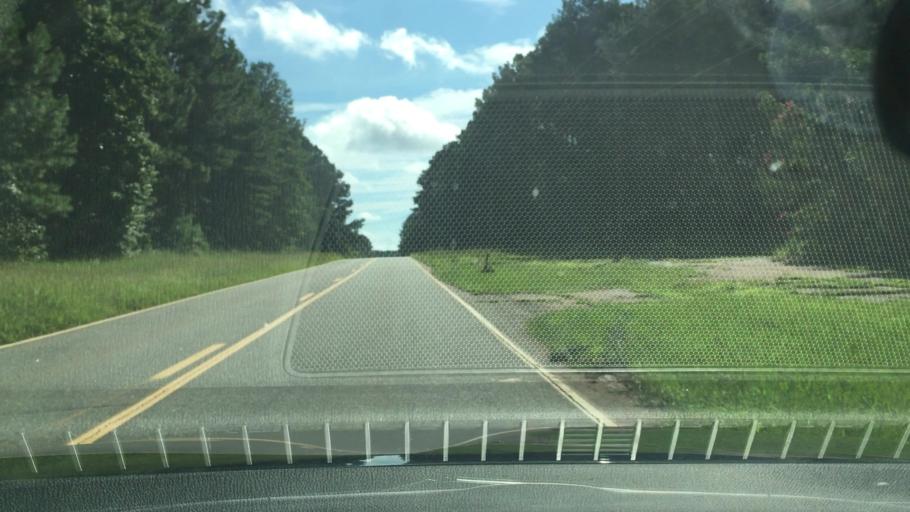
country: US
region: Georgia
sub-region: Putnam County
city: Jefferson
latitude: 33.4481
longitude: -83.3176
